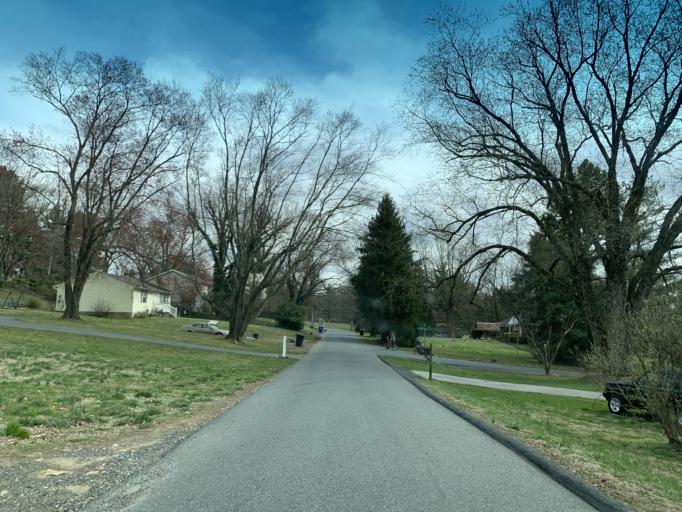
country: US
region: Maryland
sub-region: Harford County
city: North Bel Air
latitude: 39.5189
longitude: -76.3647
